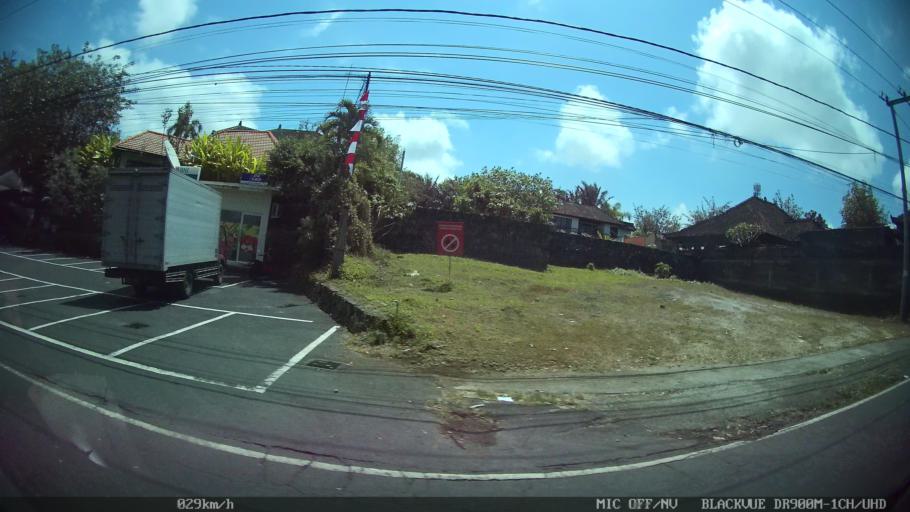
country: ID
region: Bali
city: Banjar Jabejero
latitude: -8.5920
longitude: 115.2667
